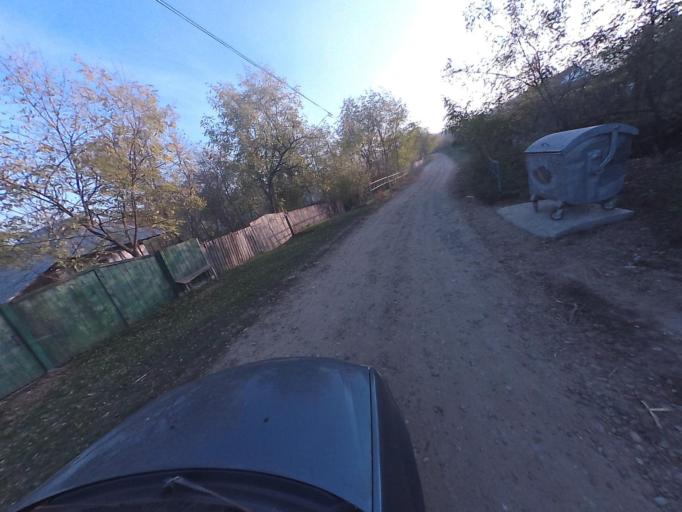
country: RO
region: Vaslui
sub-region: Comuna Bacesti
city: Bacesti
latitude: 46.8032
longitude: 27.2249
